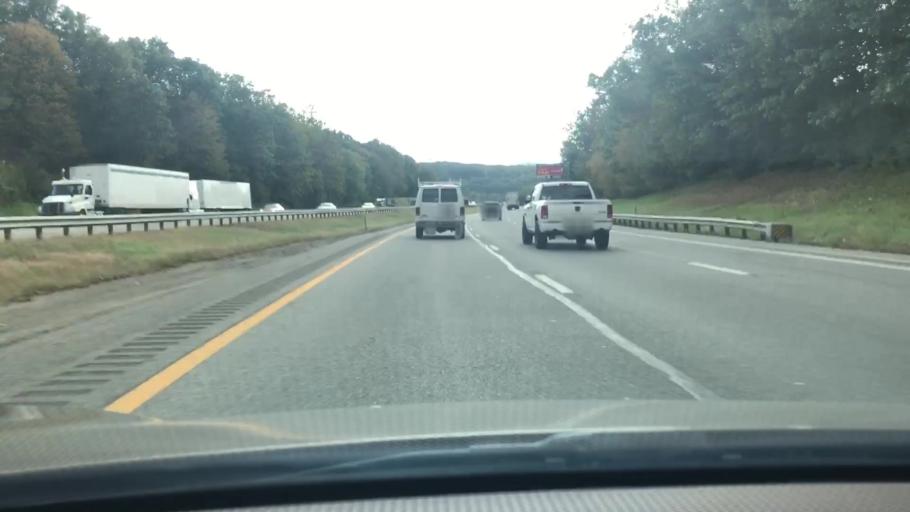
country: US
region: New York
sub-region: Rockland County
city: Sloatsburg
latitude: 41.1605
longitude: -74.1853
